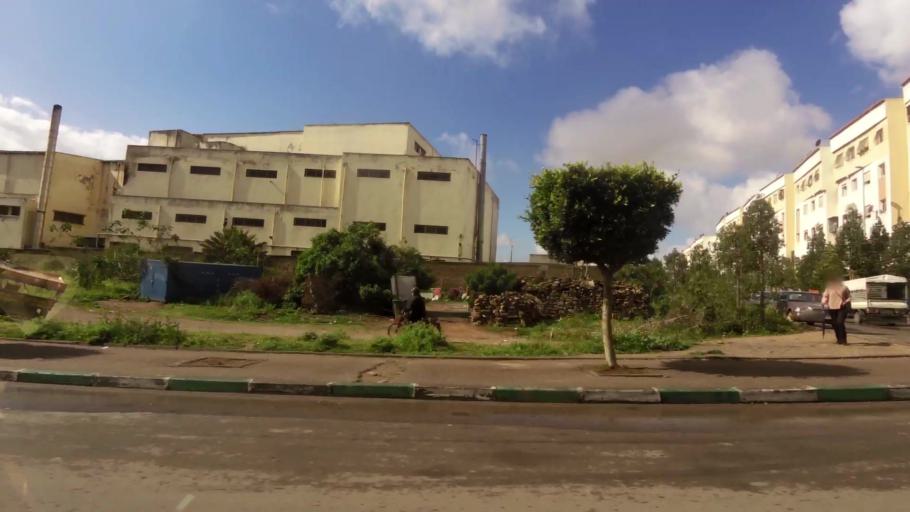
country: MA
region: Grand Casablanca
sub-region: Nouaceur
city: Bouskoura
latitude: 33.5321
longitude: -7.6788
